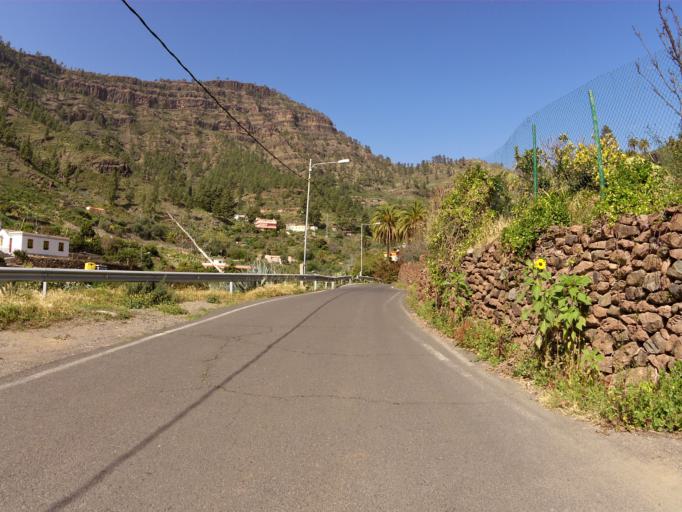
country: ES
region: Canary Islands
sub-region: Provincia de Las Palmas
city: Mogan
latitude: 27.8957
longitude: -15.6770
